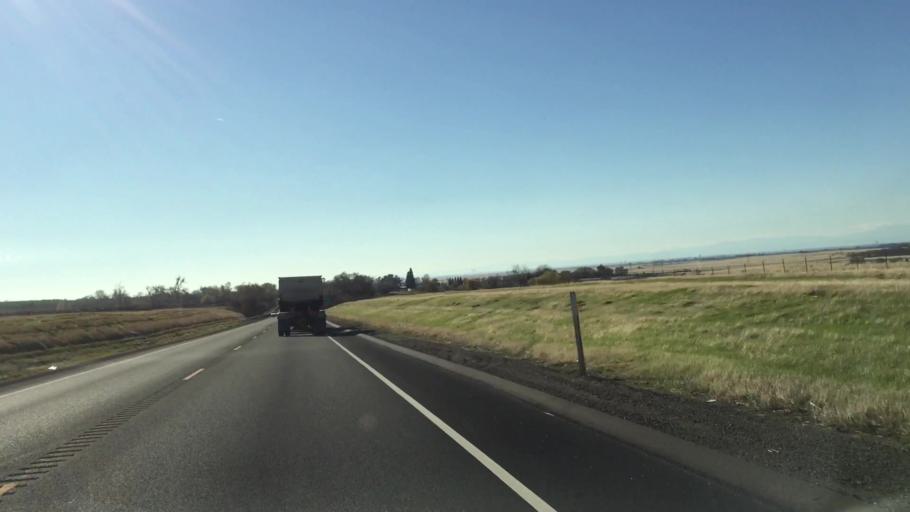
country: US
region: California
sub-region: Butte County
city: Thermalito
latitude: 39.6096
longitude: -121.6104
